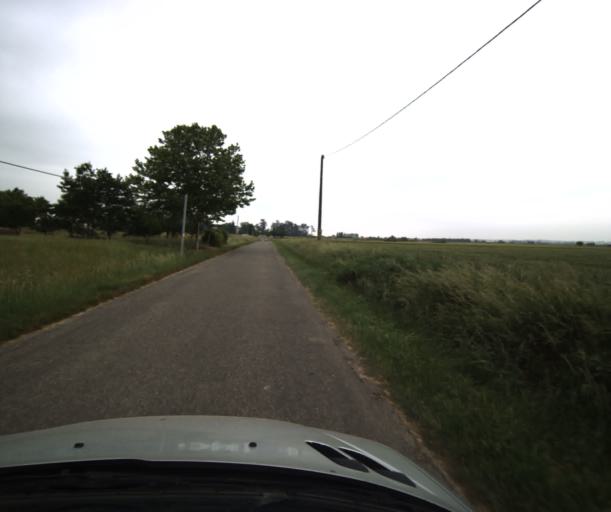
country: FR
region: Midi-Pyrenees
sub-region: Departement du Tarn-et-Garonne
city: Saint-Nicolas-de-la-Grave
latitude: 44.0477
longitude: 1.0256
